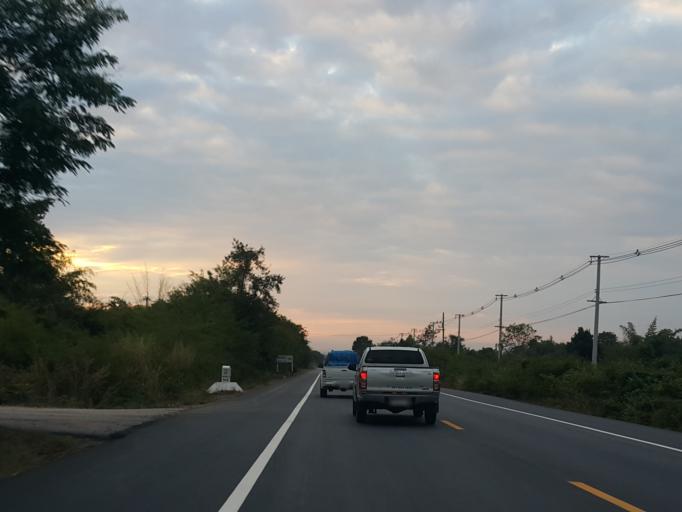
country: TH
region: Lampang
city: Lampang
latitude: 18.2510
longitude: 99.5308
